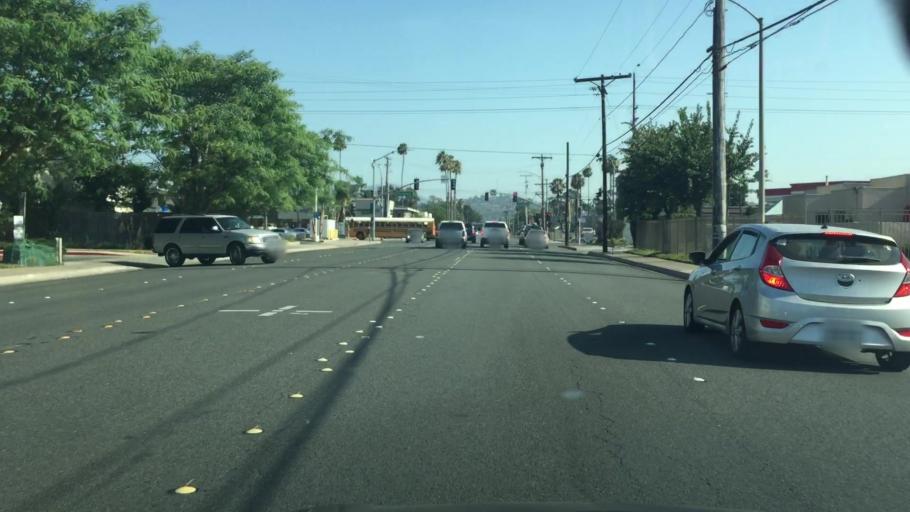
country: US
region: California
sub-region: San Diego County
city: Bostonia
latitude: 32.8087
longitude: -116.9510
